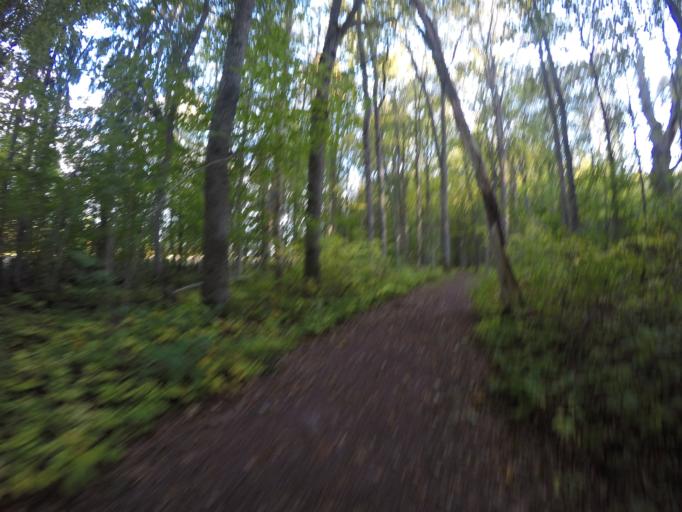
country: SE
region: Vaestmanland
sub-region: Hallstahammars Kommun
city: Kolback
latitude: 59.4790
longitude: 16.2126
